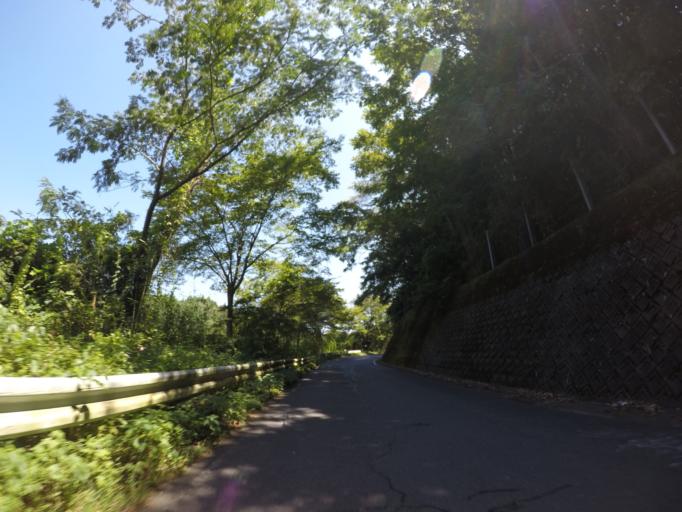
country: JP
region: Shizuoka
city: Fujinomiya
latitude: 35.2748
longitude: 138.5688
